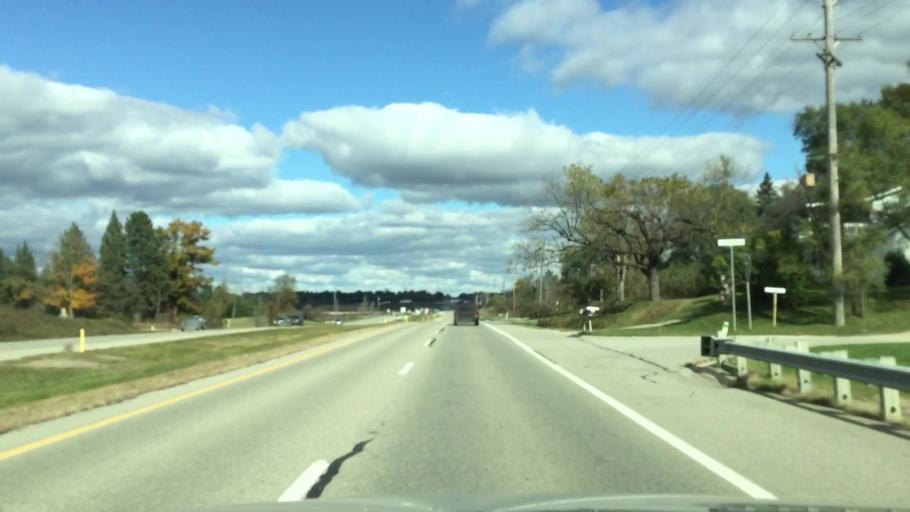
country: US
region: Michigan
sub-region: Lapeer County
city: Lapeer
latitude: 43.0092
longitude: -83.3215
